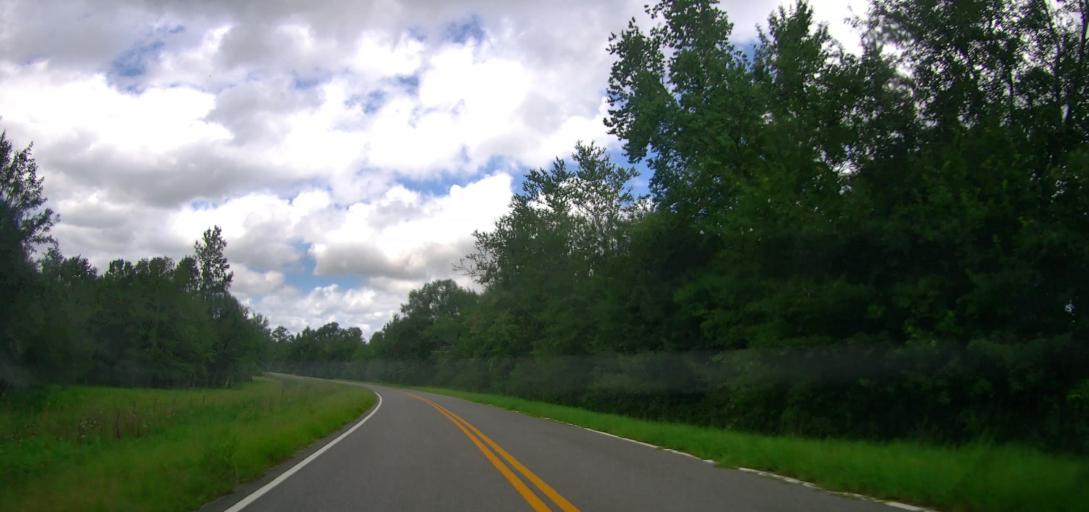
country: US
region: Georgia
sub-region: Turner County
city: Ashburn
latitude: 31.6923
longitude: -83.4764
